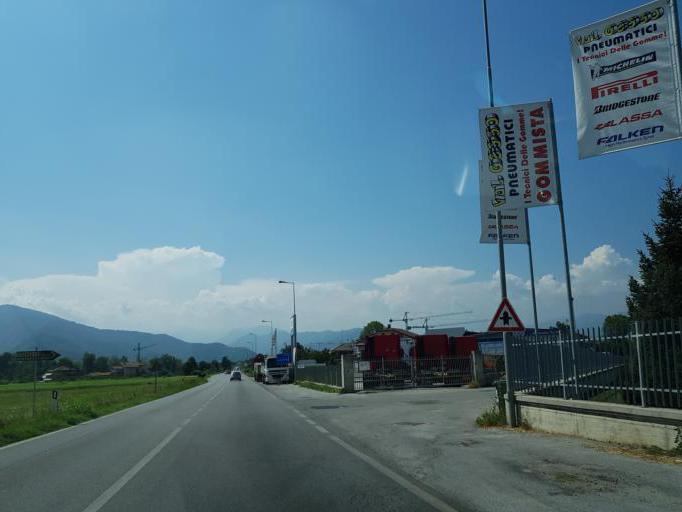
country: IT
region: Piedmont
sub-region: Provincia di Cuneo
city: San Rocco
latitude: 44.3983
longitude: 7.4681
